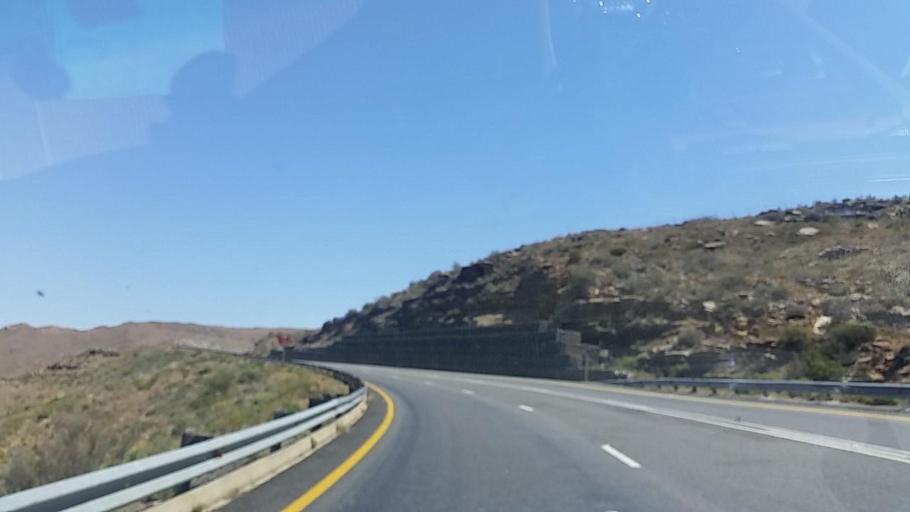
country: ZA
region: Eastern Cape
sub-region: Chris Hani District Municipality
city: Middelburg
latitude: -31.8420
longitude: 24.8699
